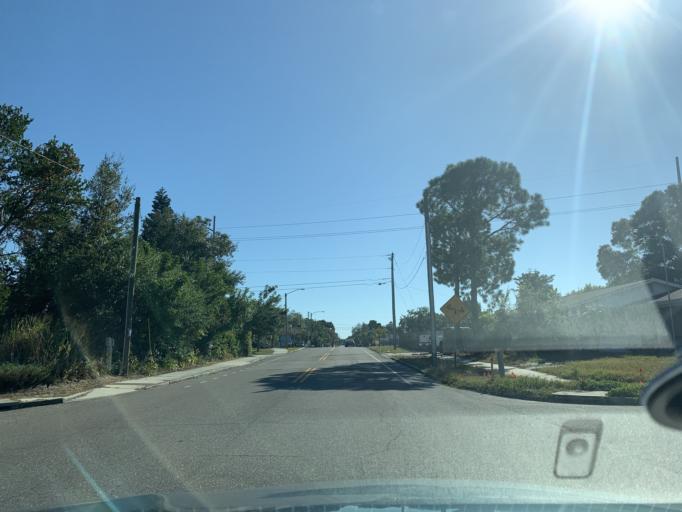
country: US
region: Florida
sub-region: Pinellas County
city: South Pasadena
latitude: 27.7674
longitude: -82.7243
